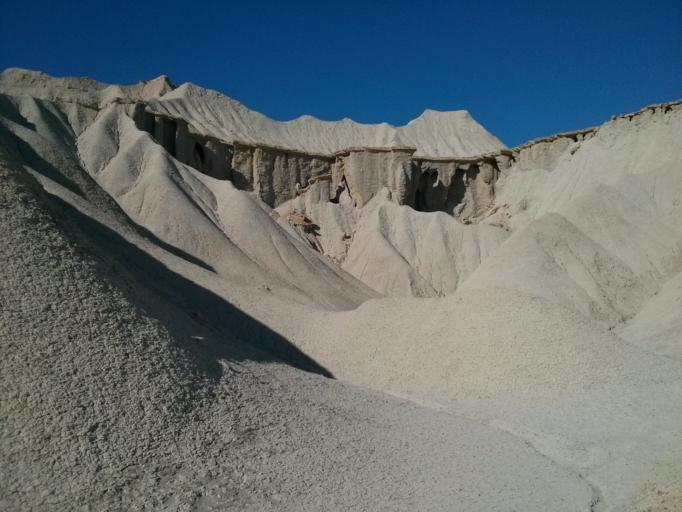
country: IR
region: Hormozgan
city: Bandar-e Khamir
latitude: 26.6698
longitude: 55.5801
